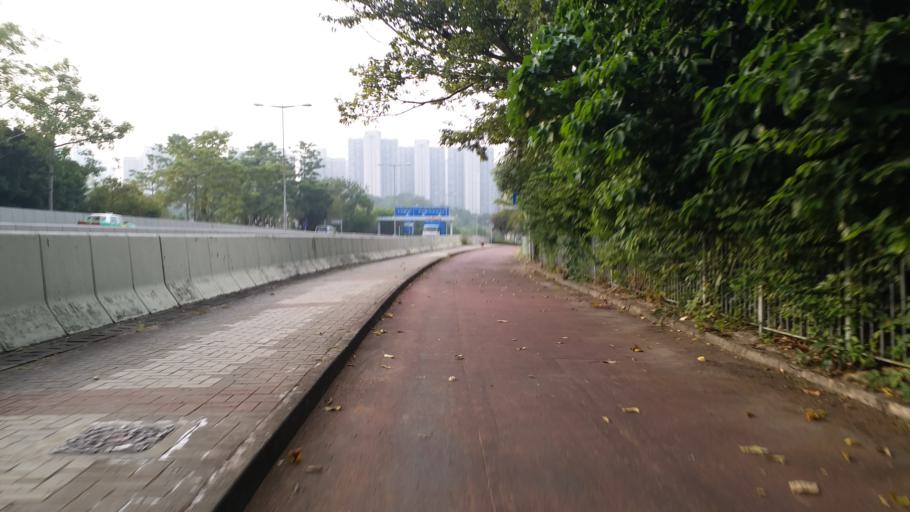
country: HK
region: Yuen Long
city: Yuen Long Kau Hui
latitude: 22.4478
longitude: 114.0122
